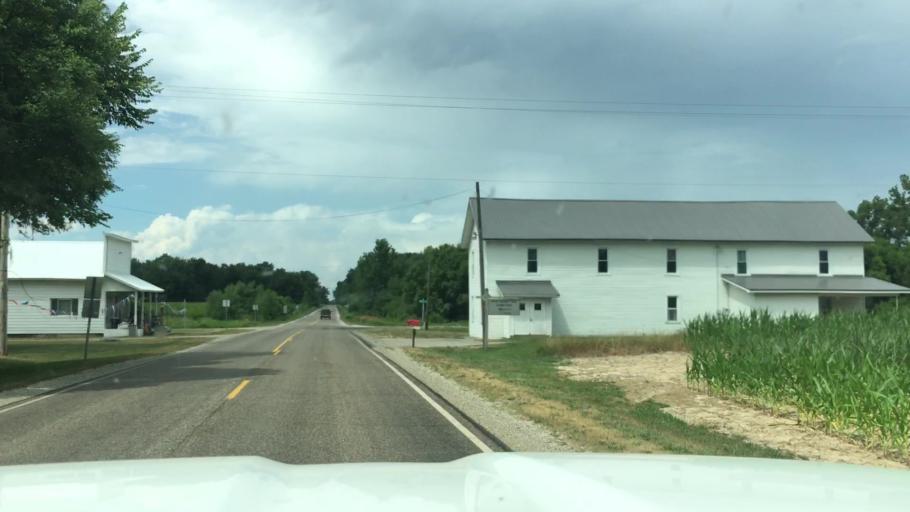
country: US
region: Michigan
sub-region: Montcalm County
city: Carson City
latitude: 43.2478
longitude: -84.7775
